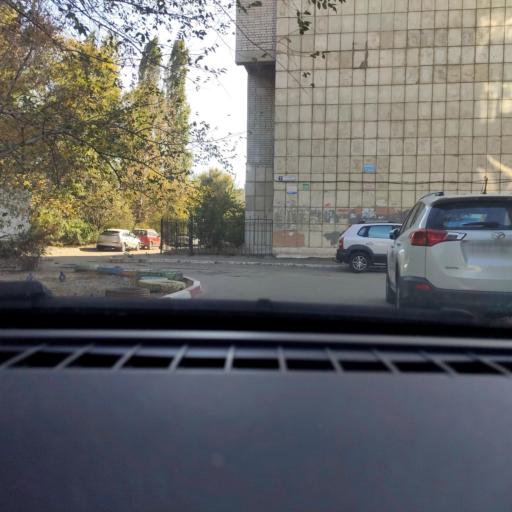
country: RU
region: Voronezj
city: Voronezh
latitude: 51.6734
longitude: 39.2458
